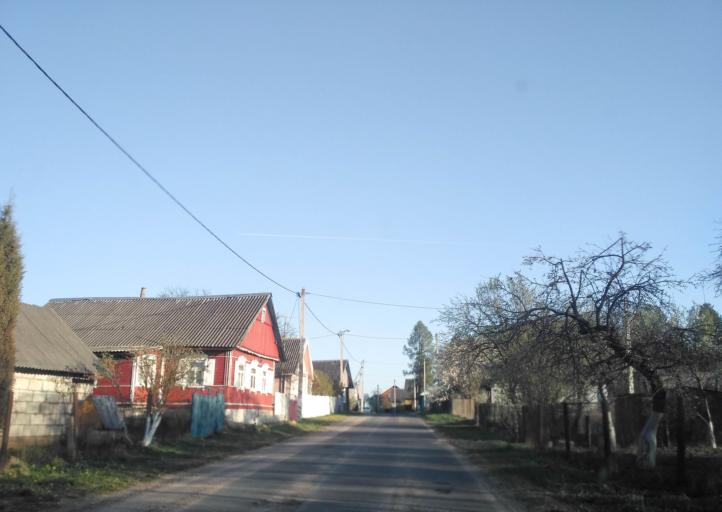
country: BY
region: Minsk
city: Pyatryshki
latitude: 54.1017
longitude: 27.1936
